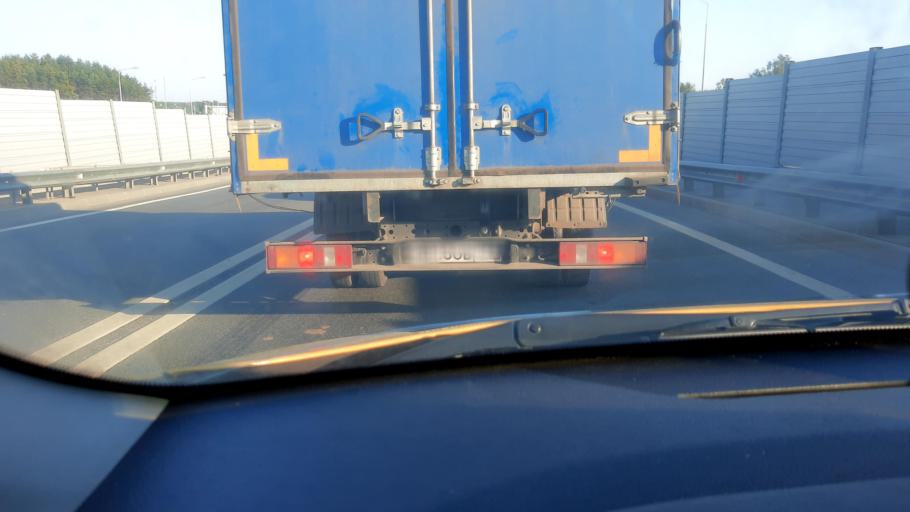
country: RU
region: Moskovskaya
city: Kokoshkino
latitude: 55.5832
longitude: 37.1257
